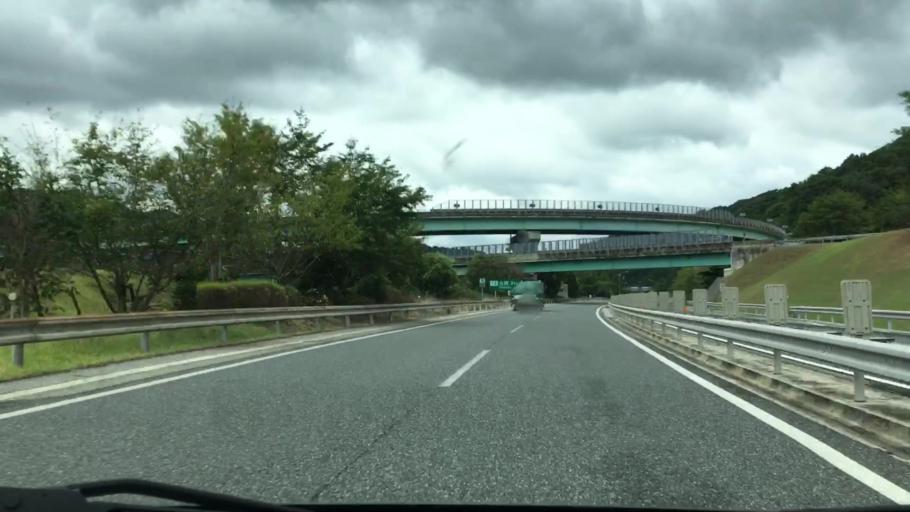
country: JP
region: Okayama
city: Takahashi
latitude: 34.9849
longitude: 133.6845
